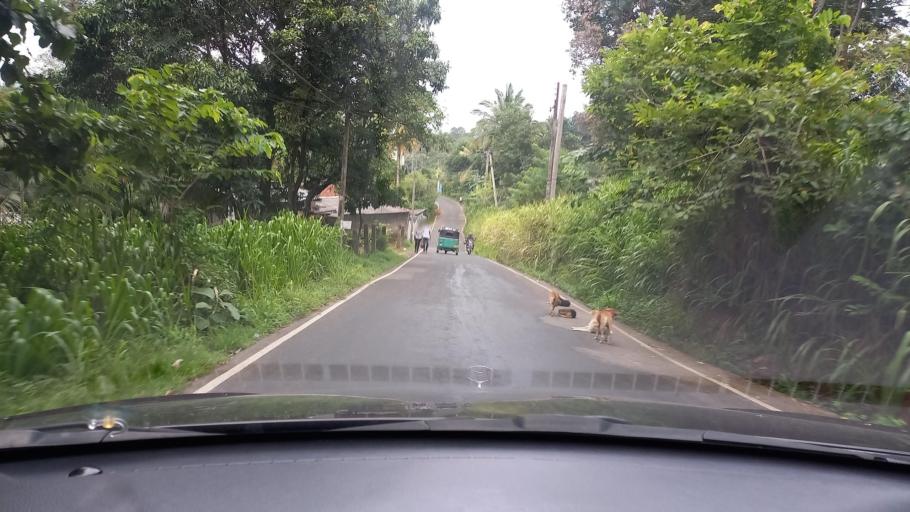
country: LK
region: Central
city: Kadugannawa
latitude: 7.2596
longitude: 80.3526
